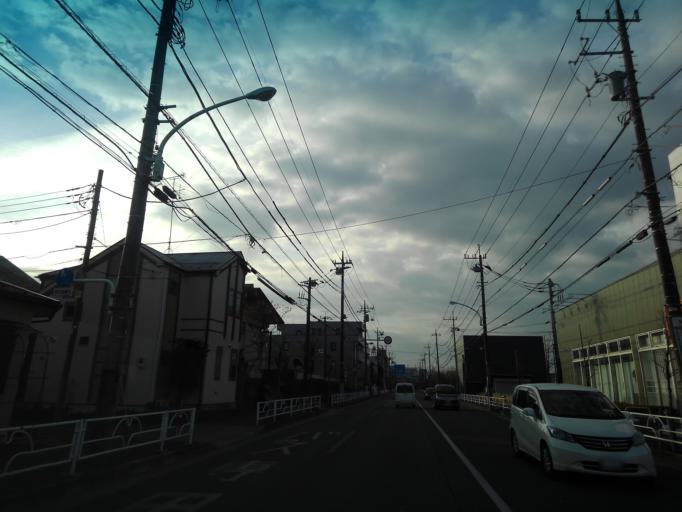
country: JP
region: Tokyo
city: Tanashicho
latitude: 35.7329
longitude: 139.5126
